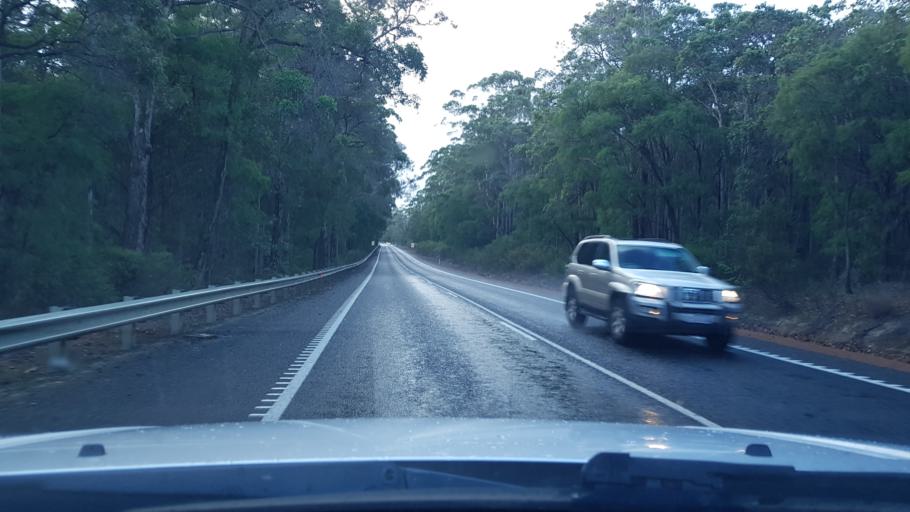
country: AU
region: Western Australia
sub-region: Augusta-Margaret River Shire
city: Margaret River
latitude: -33.9136
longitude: 115.0834
